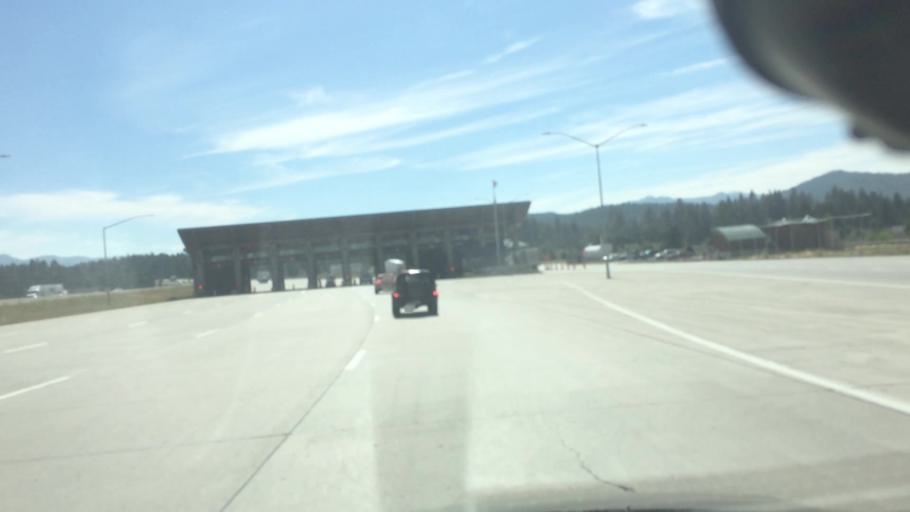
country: US
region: California
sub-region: Nevada County
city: Truckee
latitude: 39.3611
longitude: -120.1350
